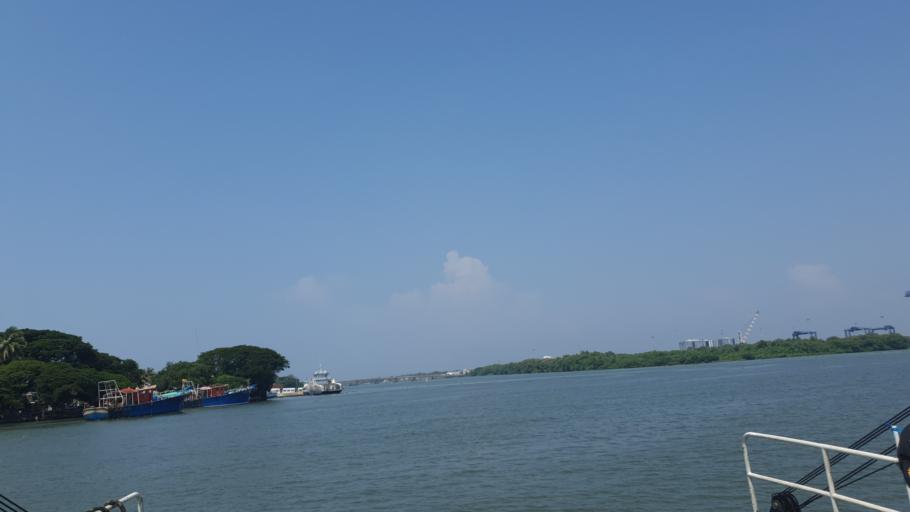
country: IN
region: Kerala
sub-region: Ernakulam
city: Cochin
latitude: 9.9711
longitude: 76.2450
